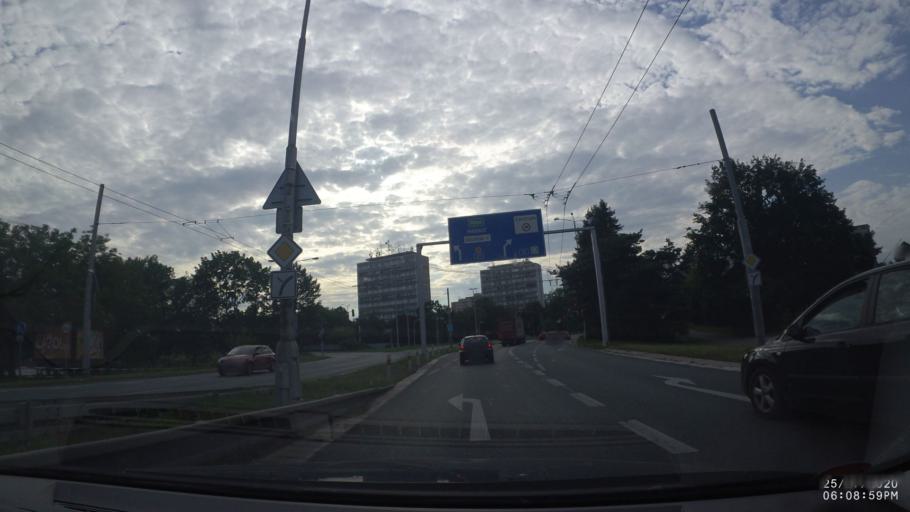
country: CZ
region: Kralovehradecky
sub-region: Okres Hradec Kralove
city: Hradec Kralove
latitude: 50.2028
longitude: 15.8233
